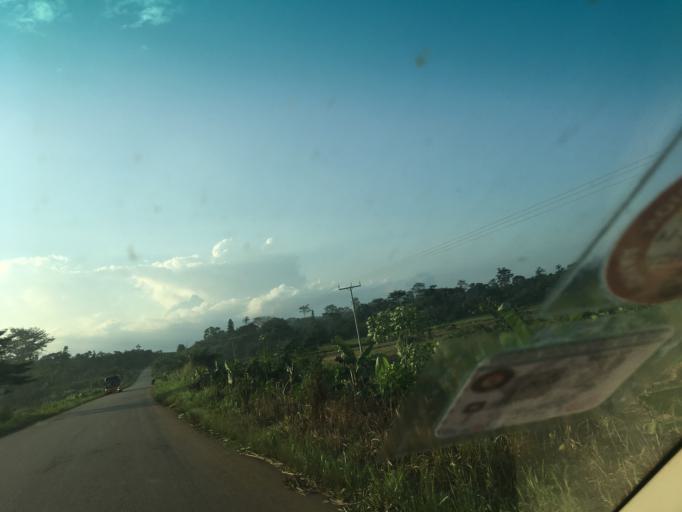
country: GH
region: Western
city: Bibiani
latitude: 6.5757
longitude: -2.3740
